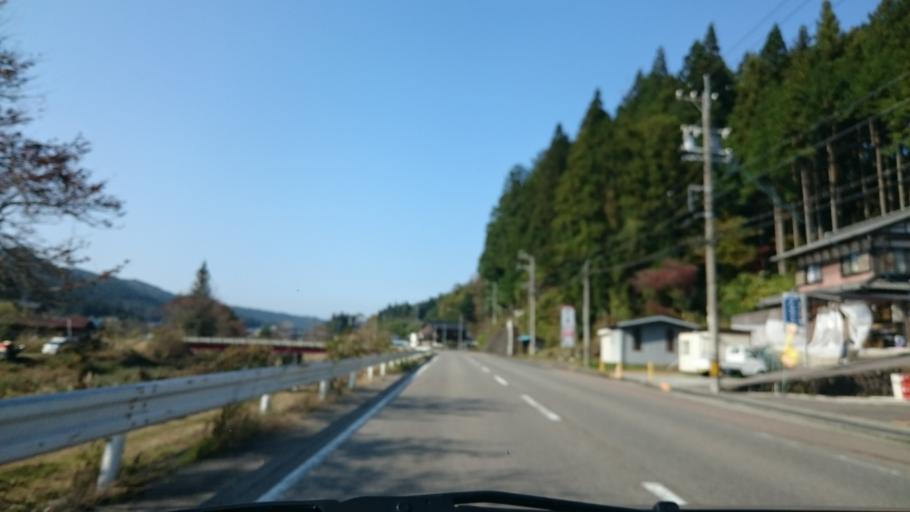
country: JP
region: Gifu
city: Nakatsugawa
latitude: 35.7230
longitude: 137.3561
